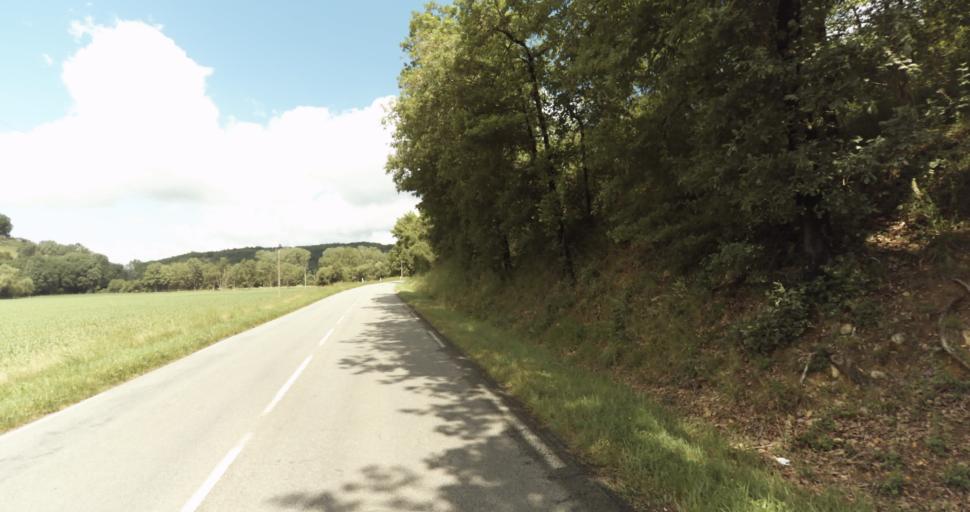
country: FR
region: Aquitaine
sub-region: Departement de la Dordogne
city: Beaumont-du-Perigord
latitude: 44.7941
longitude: 0.7551
